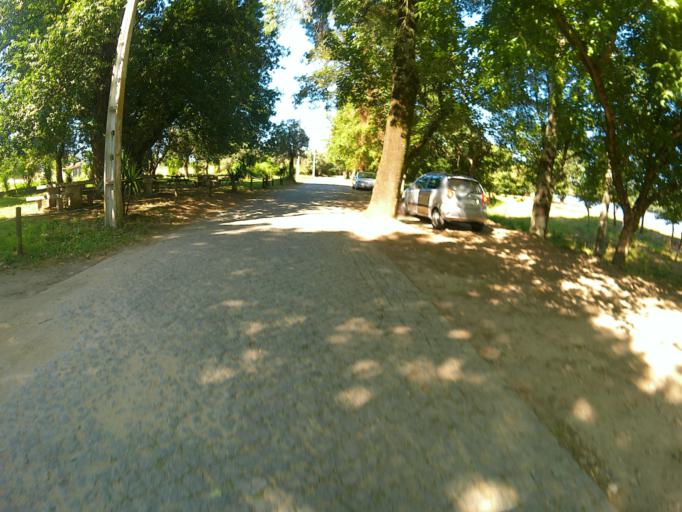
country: PT
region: Viana do Castelo
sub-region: Ponte de Lima
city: Ponte de Lima
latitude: 41.7252
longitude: -8.6732
